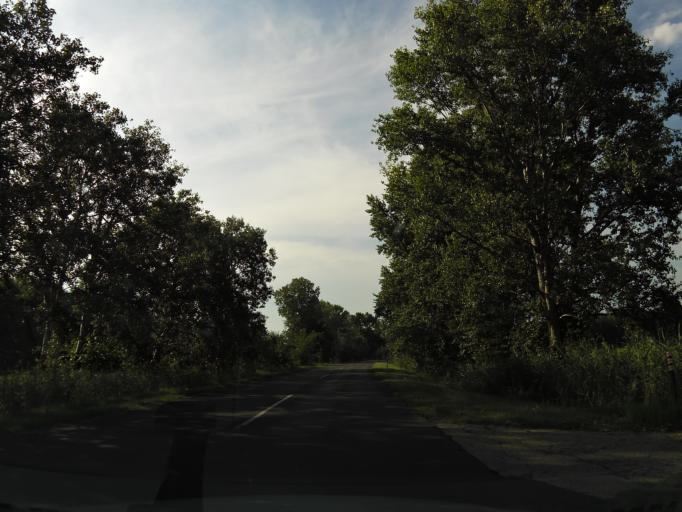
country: HU
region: Csongrad
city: Balastya
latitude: 46.3947
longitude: 20.0285
